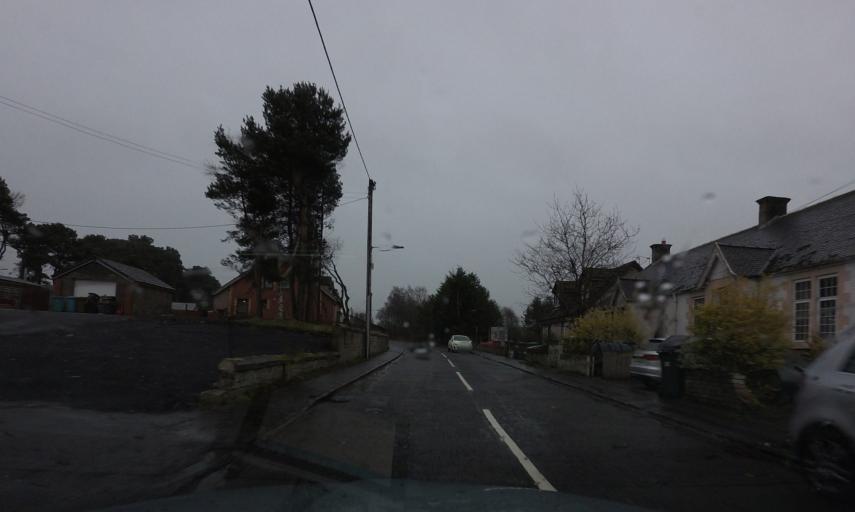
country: GB
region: Scotland
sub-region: North Lanarkshire
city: Shotts
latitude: 55.8065
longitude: -3.8337
